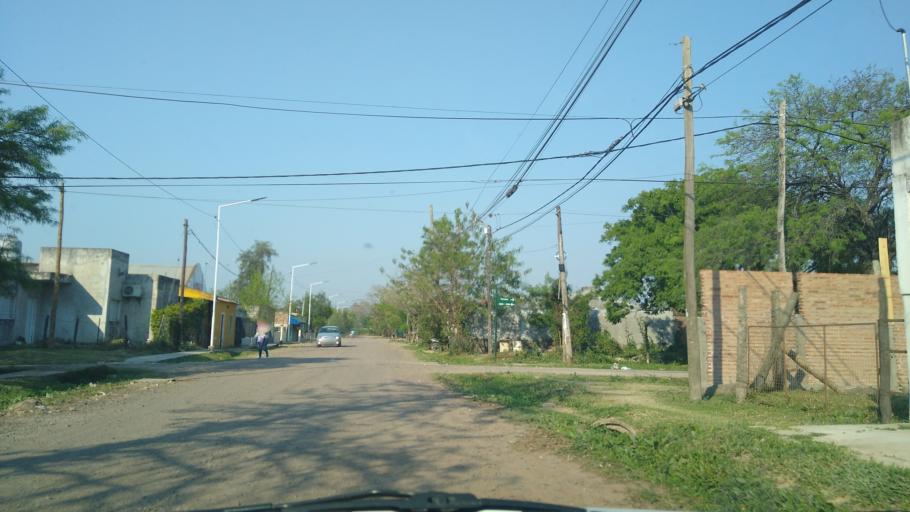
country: AR
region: Chaco
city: Barranqueras
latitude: -27.4754
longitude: -58.9494
